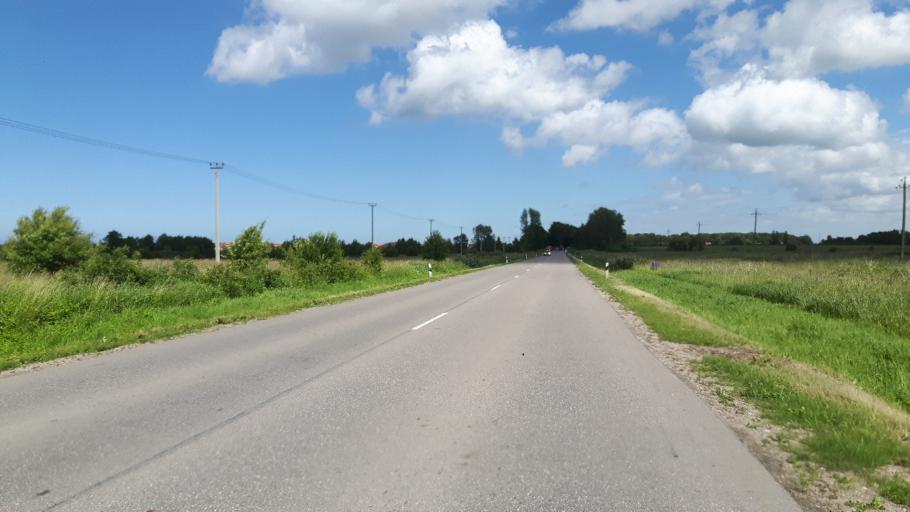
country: RU
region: Kaliningrad
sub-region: Zelenogradskiy Rayon
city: Zelenogradsk
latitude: 54.9324
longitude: 20.4326
